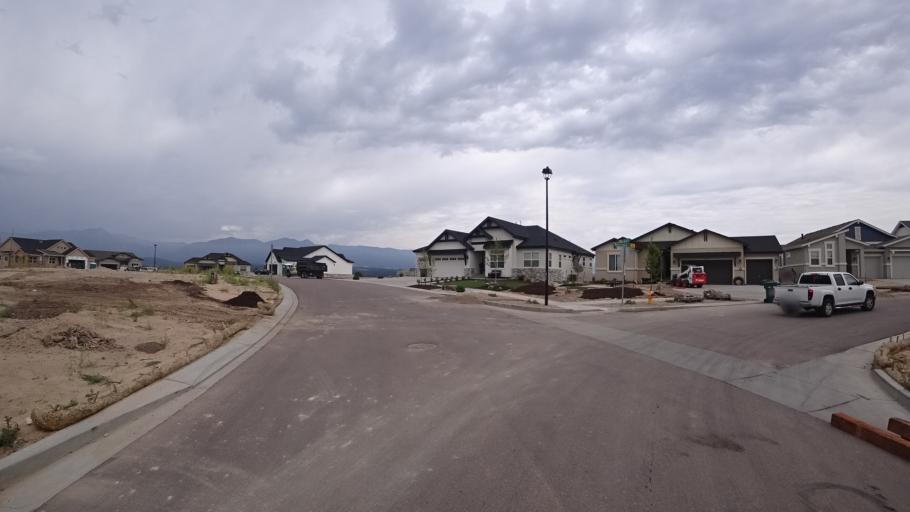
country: US
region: Colorado
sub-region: El Paso County
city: Gleneagle
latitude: 39.0060
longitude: -104.8102
